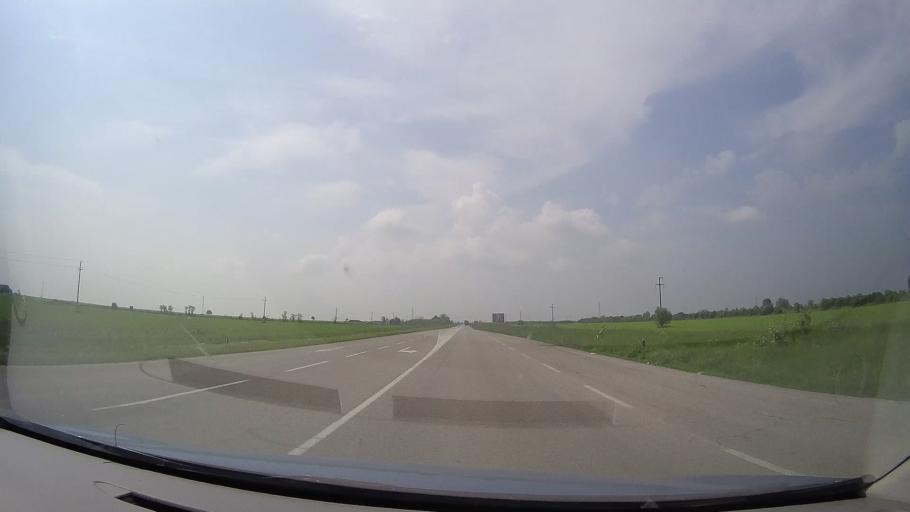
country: RS
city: Debeljaca
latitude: 45.0763
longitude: 20.6409
